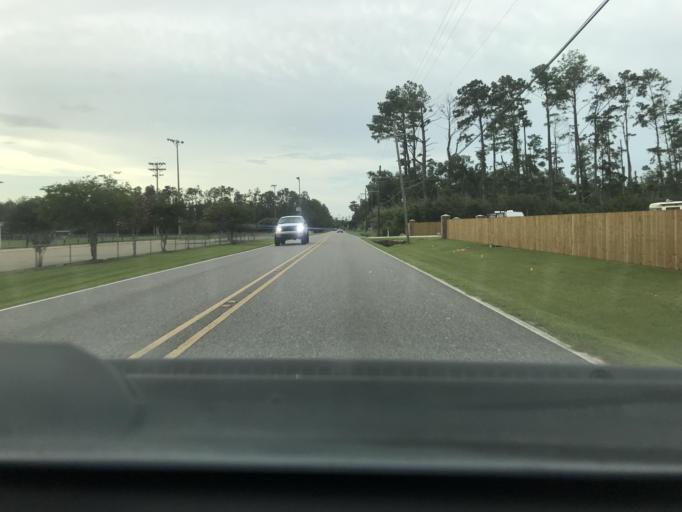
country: US
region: Louisiana
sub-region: Calcasieu Parish
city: Westlake
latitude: 30.2812
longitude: -93.2582
